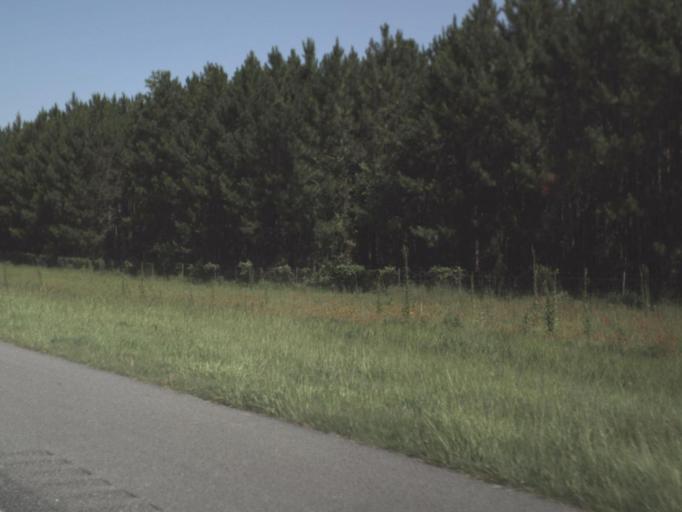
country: US
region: Florida
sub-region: Suwannee County
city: Live Oak
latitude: 30.3528
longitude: -83.0355
